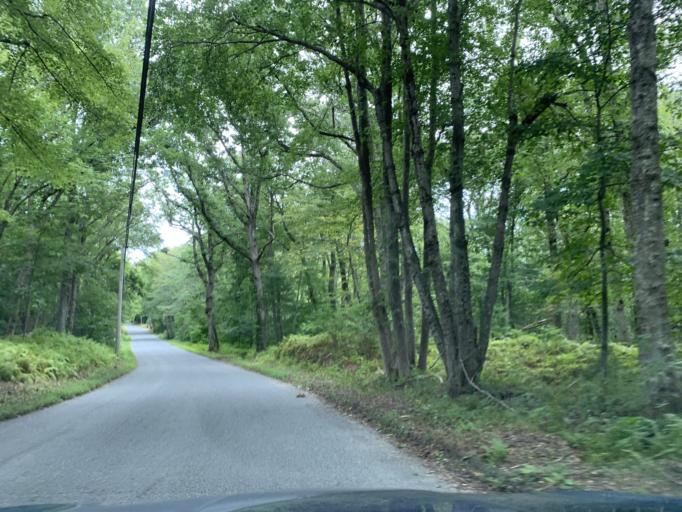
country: US
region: Rhode Island
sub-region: Kent County
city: West Greenwich
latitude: 41.5790
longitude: -71.6158
